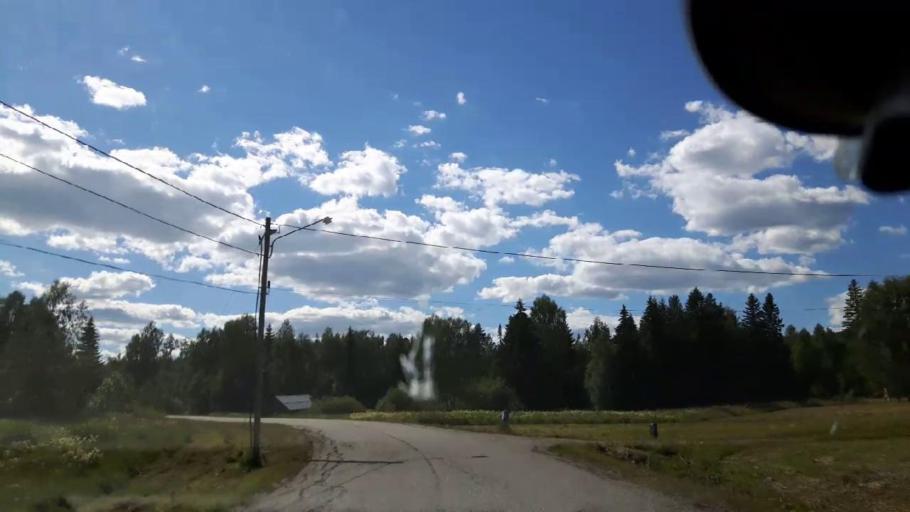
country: SE
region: Vaesternorrland
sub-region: Ange Kommun
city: Fransta
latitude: 62.7828
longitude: 15.9973
